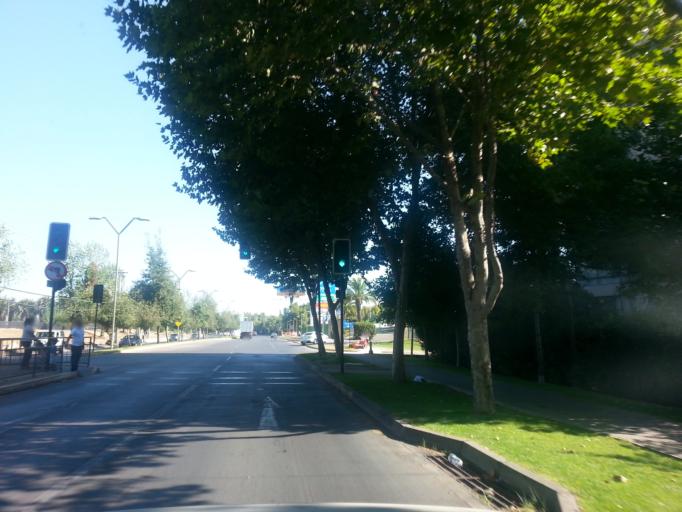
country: CL
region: Santiago Metropolitan
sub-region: Provincia de Santiago
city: Villa Presidente Frei, Nunoa, Santiago, Chile
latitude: -33.4268
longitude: -70.5388
